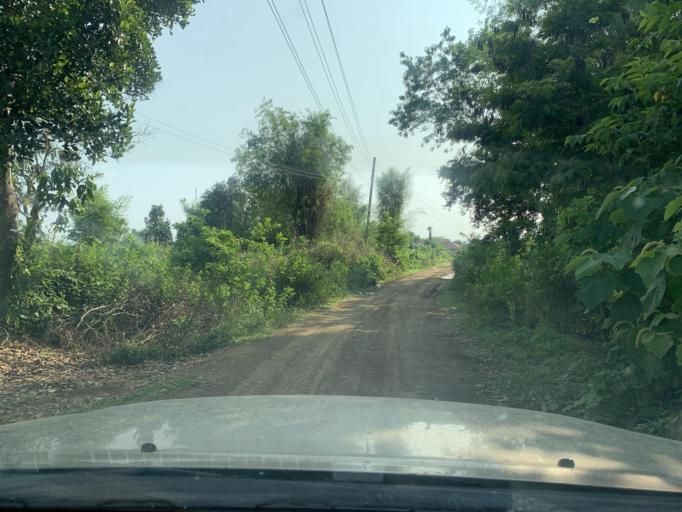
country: TH
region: Uttaradit
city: Ban Khok
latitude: 18.2836
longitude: 101.3169
